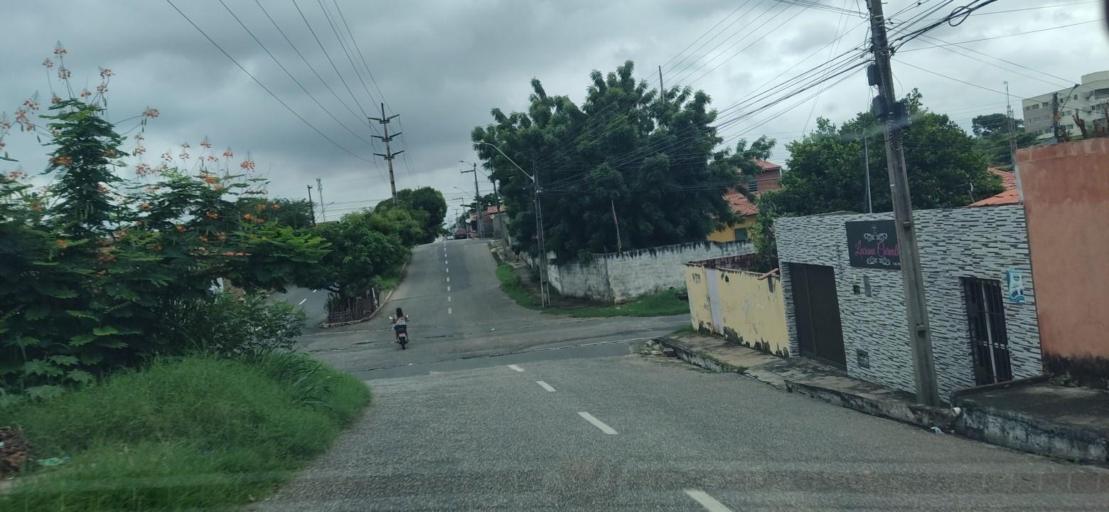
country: BR
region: Piaui
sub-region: Teresina
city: Teresina
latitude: -5.0603
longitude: -42.7515
